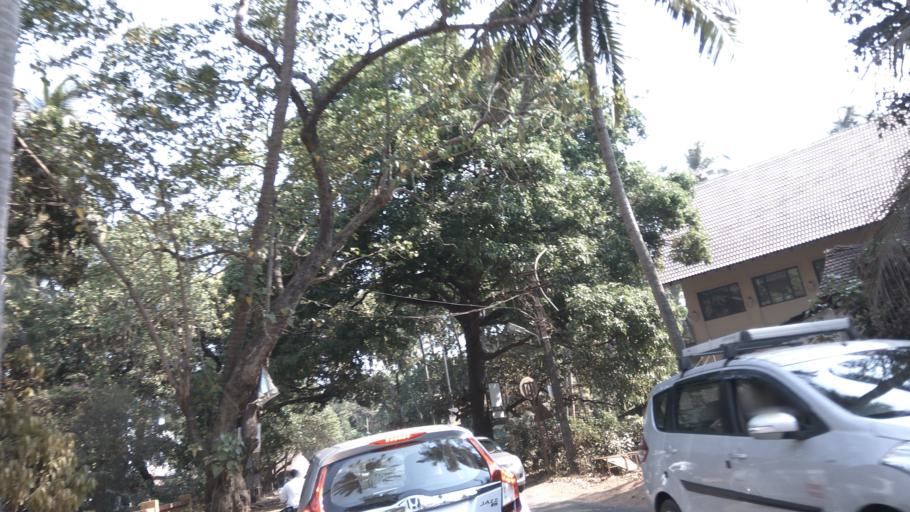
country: IN
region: Goa
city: Calangute
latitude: 15.5383
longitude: 73.7660
